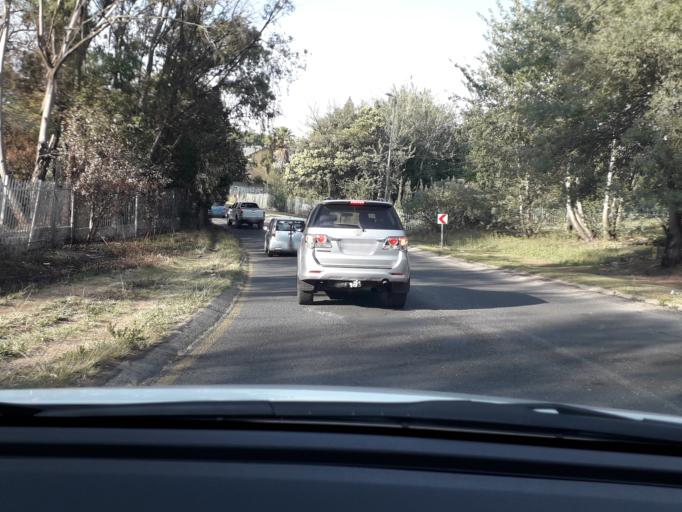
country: ZA
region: Gauteng
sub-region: West Rand District Municipality
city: Muldersdriseloop
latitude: -26.0739
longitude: 27.9459
